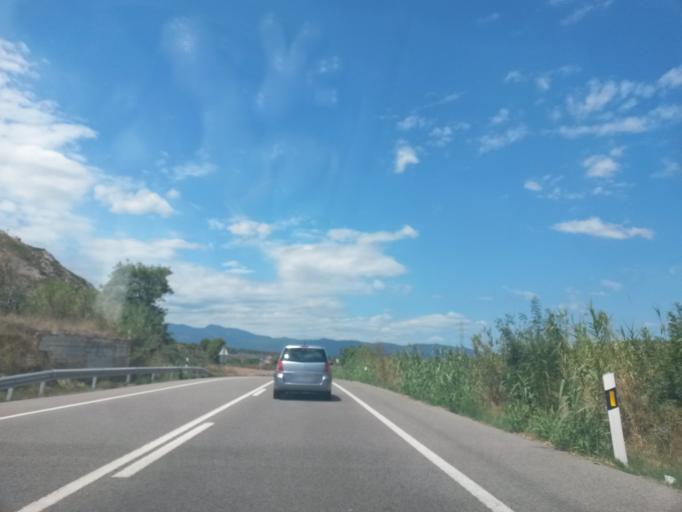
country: ES
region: Catalonia
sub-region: Provincia de Girona
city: Biure
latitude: 42.3468
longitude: 2.9126
